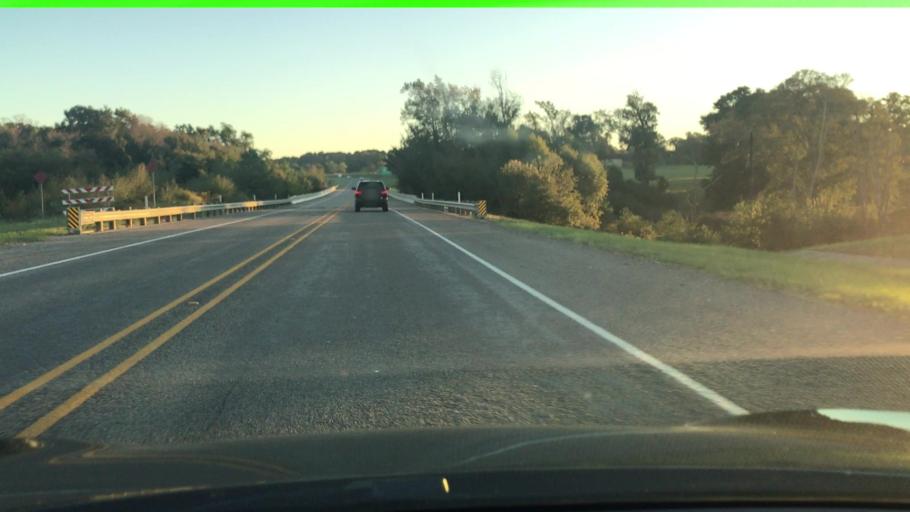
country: US
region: Texas
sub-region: Henderson County
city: Athens
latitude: 32.1771
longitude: -95.8201
